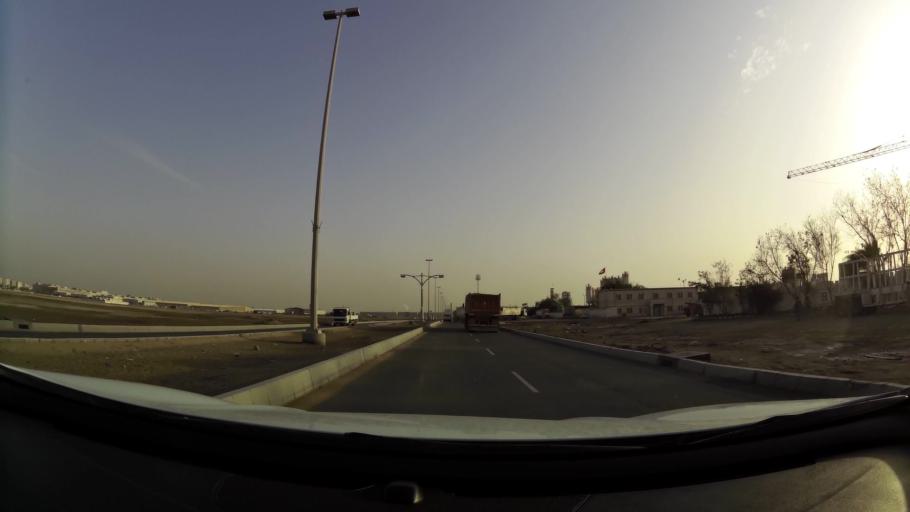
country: AE
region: Abu Dhabi
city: Abu Dhabi
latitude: 24.3425
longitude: 54.5124
